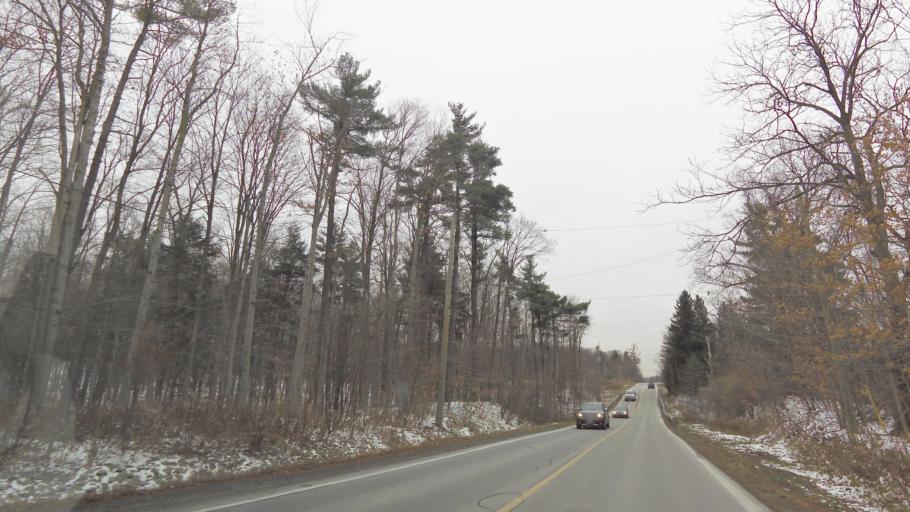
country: CA
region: Ontario
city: Vaughan
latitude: 43.8317
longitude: -79.5846
